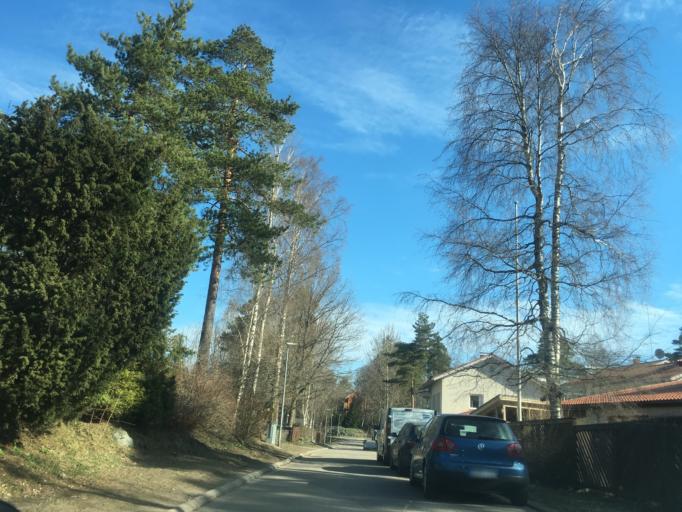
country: FI
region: Uusimaa
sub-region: Helsinki
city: Espoo
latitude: 60.1425
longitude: 24.6435
